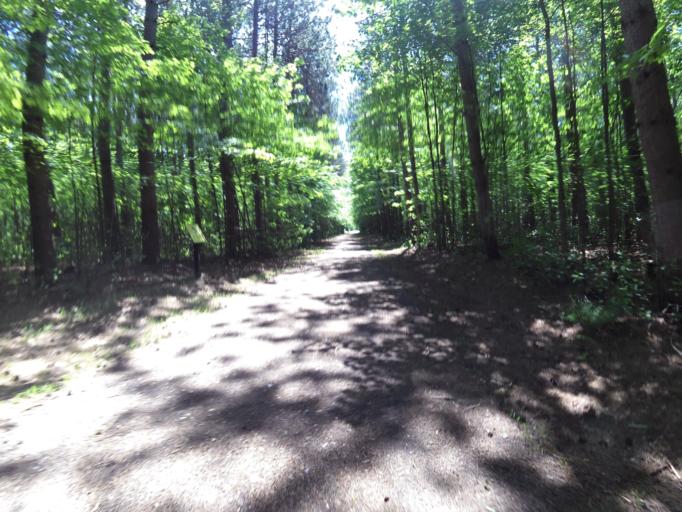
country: CA
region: Ontario
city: Ottawa
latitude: 45.3563
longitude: -75.5941
